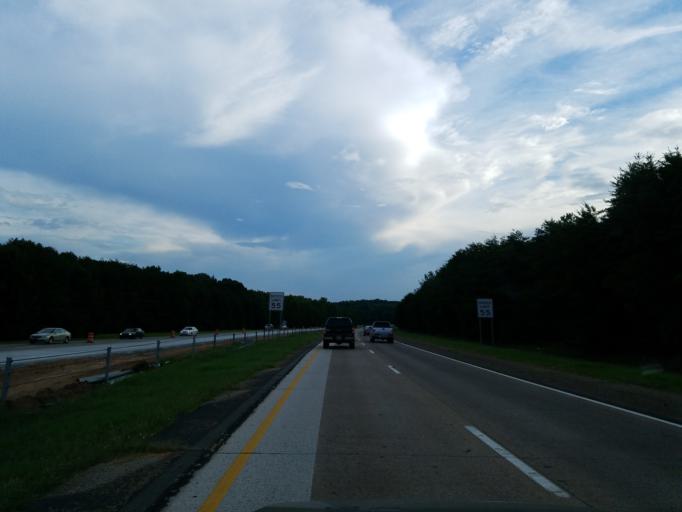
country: US
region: Georgia
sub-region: Forsyth County
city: Cumming
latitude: 34.2286
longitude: -84.1023
